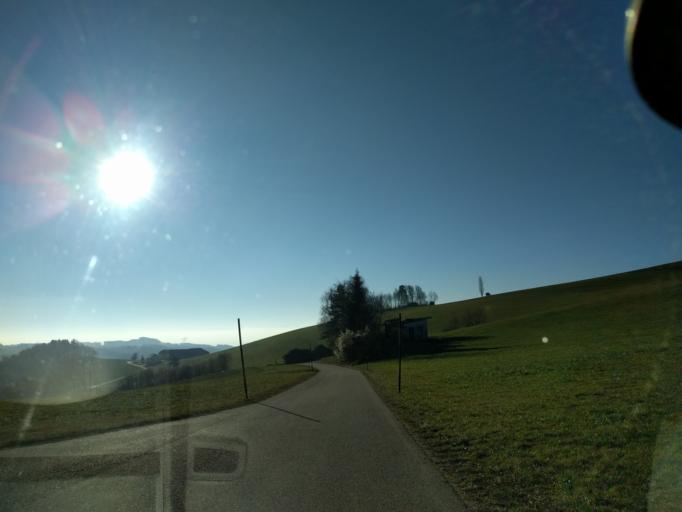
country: AT
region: Upper Austria
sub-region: Politischer Bezirk Urfahr-Umgebung
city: Kirchschlag bei Linz
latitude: 48.4031
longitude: 14.2878
